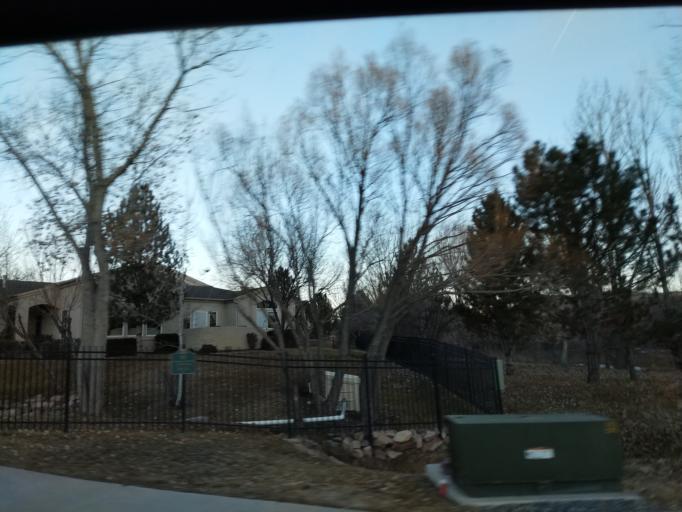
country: US
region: Colorado
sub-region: Mesa County
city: Grand Junction
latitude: 39.1046
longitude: -108.5523
